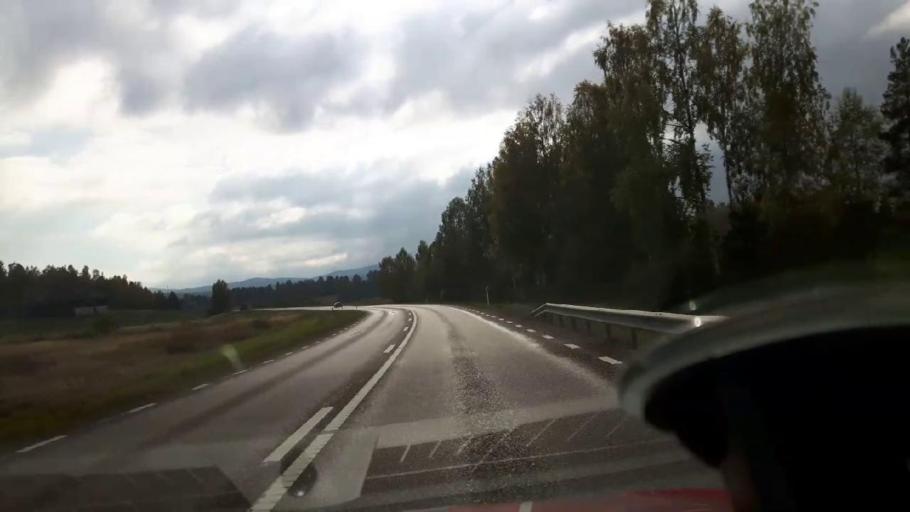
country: SE
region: Gaevleborg
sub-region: Bollnas Kommun
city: Kilafors
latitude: 61.2408
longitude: 16.5506
